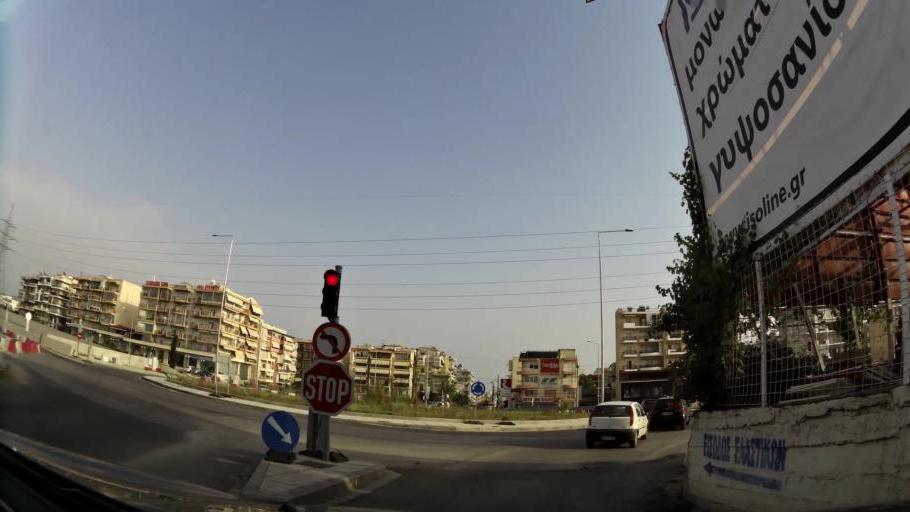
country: GR
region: Central Macedonia
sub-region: Nomos Thessalonikis
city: Evosmos
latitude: 40.6782
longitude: 22.9061
